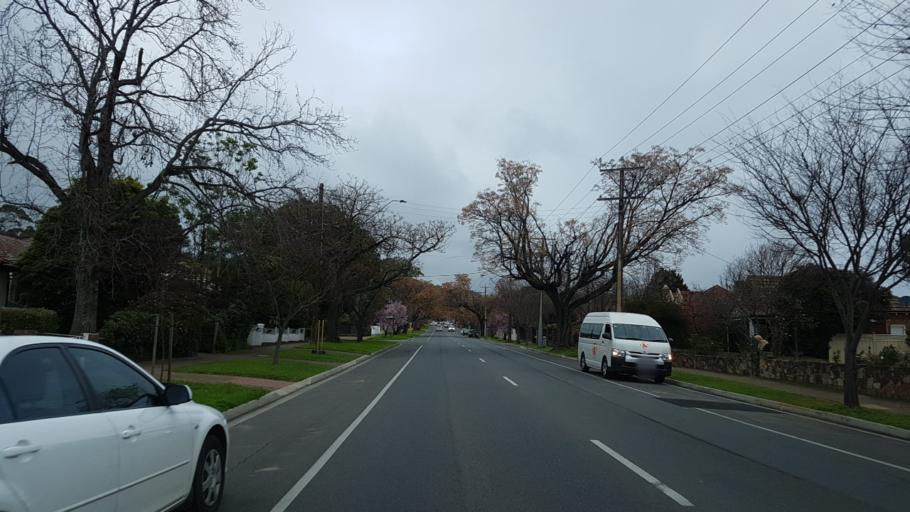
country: AU
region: South Australia
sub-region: Burnside
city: Tusmore
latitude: -34.9419
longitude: 138.6517
